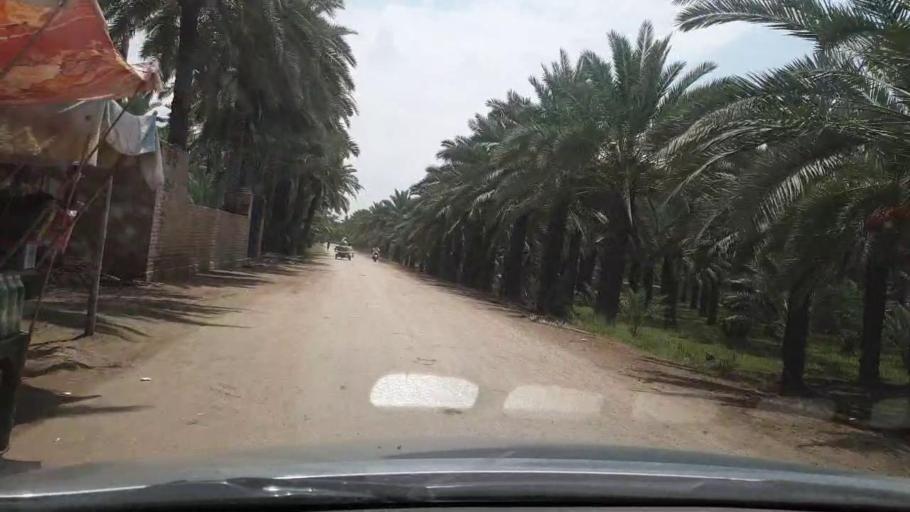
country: PK
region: Sindh
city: Khairpur
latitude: 27.4351
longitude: 68.7669
